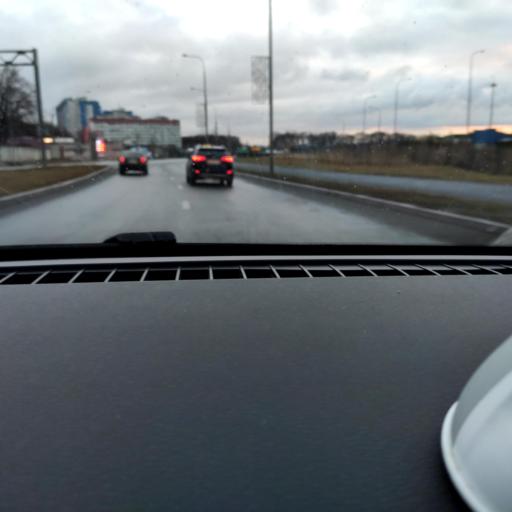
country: RU
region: Samara
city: Petra-Dubrava
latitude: 53.2782
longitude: 50.2552
